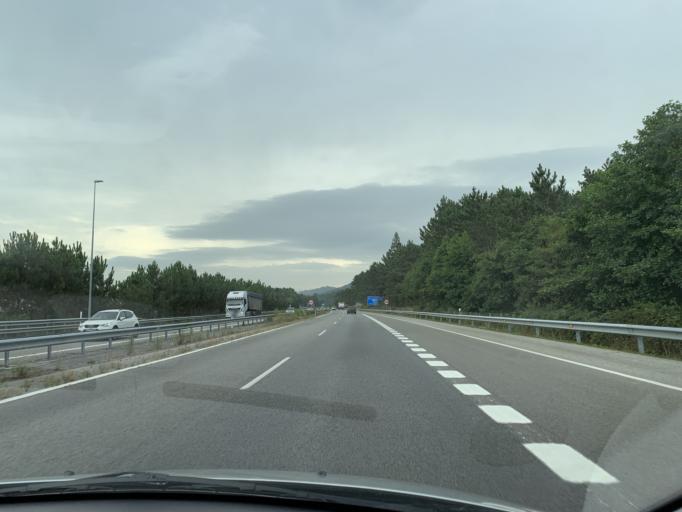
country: ES
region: Asturias
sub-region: Province of Asturias
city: Salas
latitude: 43.5492
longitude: -6.3247
